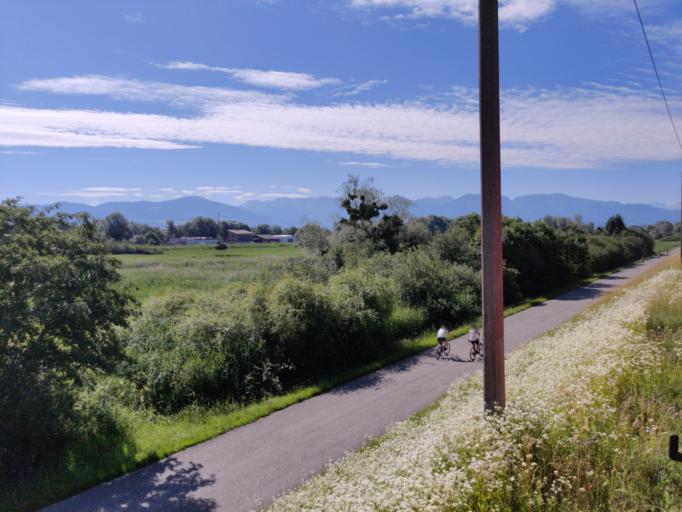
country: AT
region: Vorarlberg
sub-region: Politischer Bezirk Bregenz
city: Fussach
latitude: 47.4844
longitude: 9.6716
